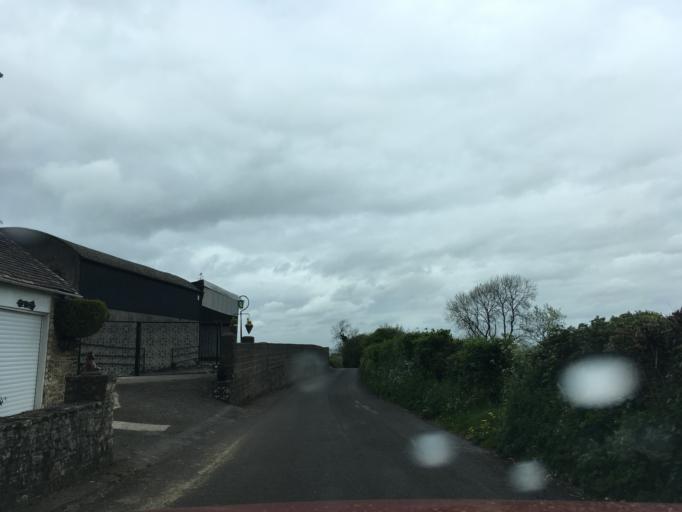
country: GB
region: England
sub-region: Bath and North East Somerset
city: Clutton
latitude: 51.3436
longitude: -2.5387
